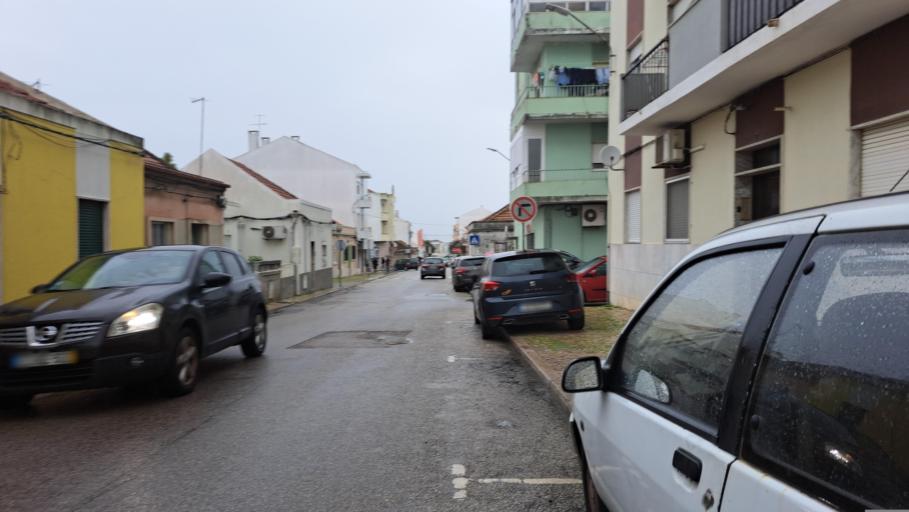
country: PT
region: Setubal
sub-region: Moita
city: Alhos Vedros
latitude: 38.6557
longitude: -9.0453
